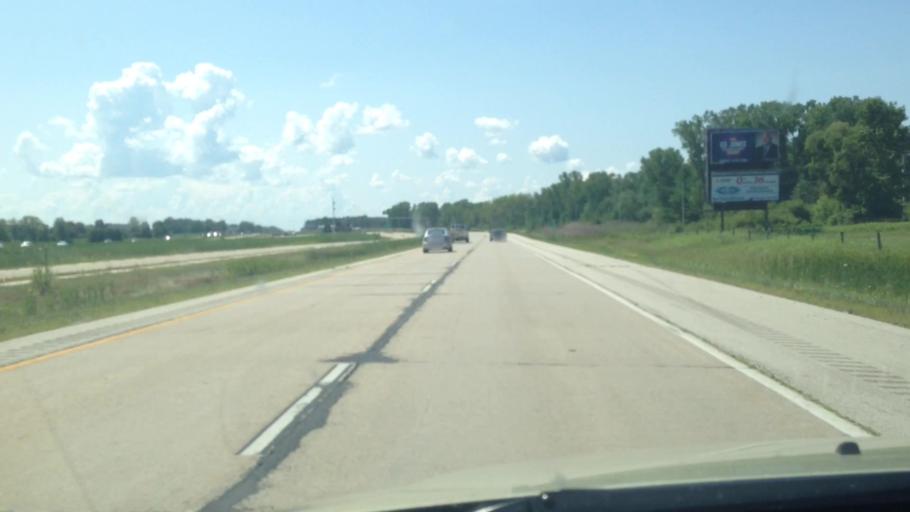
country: US
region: Wisconsin
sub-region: Brown County
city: Suamico
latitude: 44.7477
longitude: -88.0514
